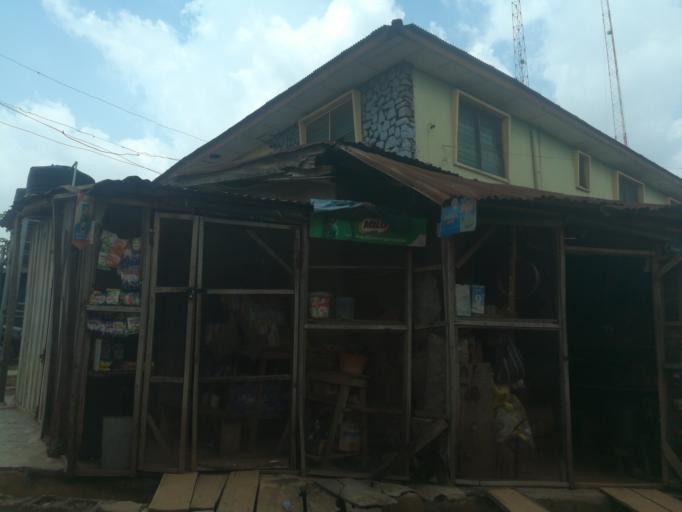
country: NG
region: Oyo
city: Ibadan
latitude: 7.3507
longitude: 3.8755
